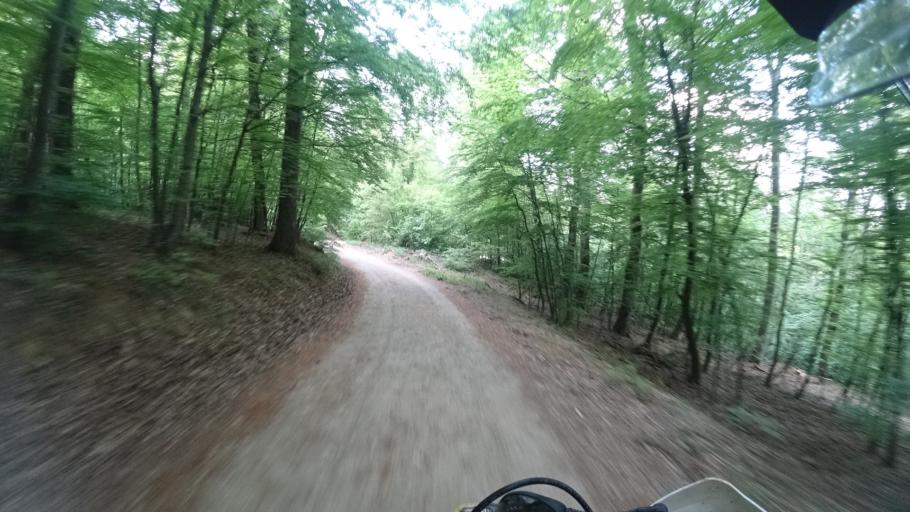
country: HR
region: Grad Zagreb
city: Stenjevec
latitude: 45.8515
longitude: 15.8898
